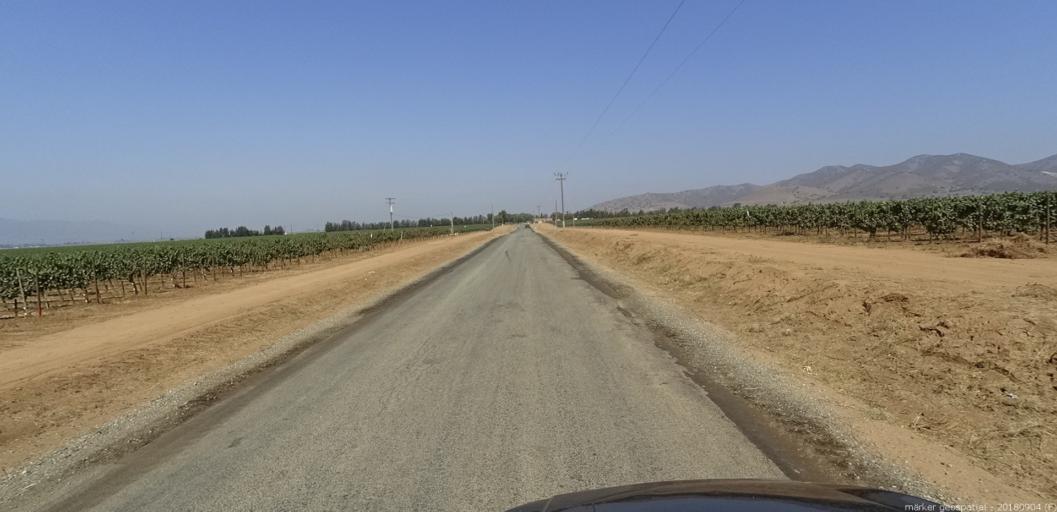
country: US
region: California
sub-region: Monterey County
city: Gonzales
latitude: 36.5453
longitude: -121.4319
